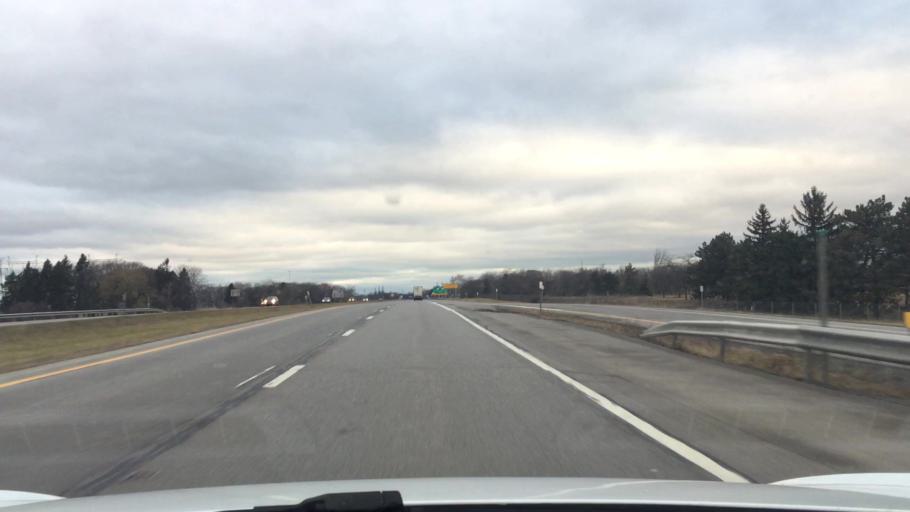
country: US
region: New York
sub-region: Niagara County
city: Lewiston
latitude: 43.1315
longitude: -79.0189
